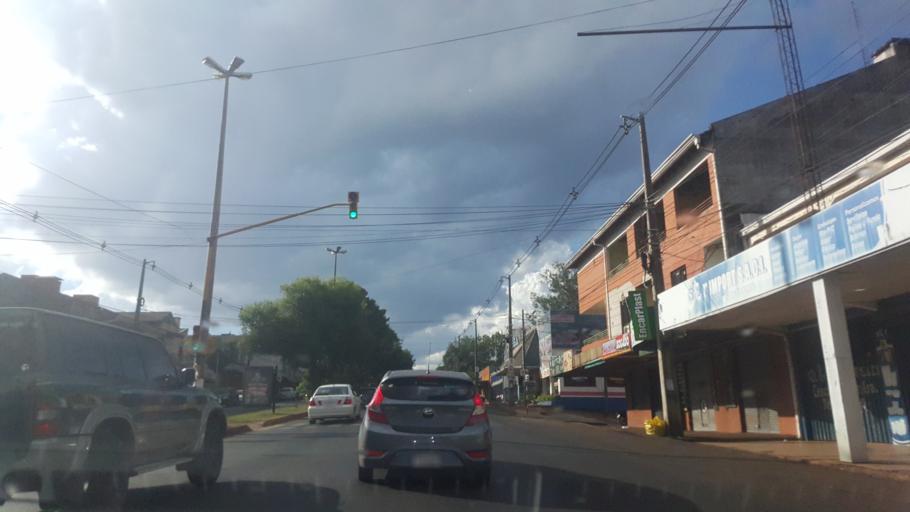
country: PY
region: Itapua
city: Encarnacion
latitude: -27.3313
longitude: -55.8588
